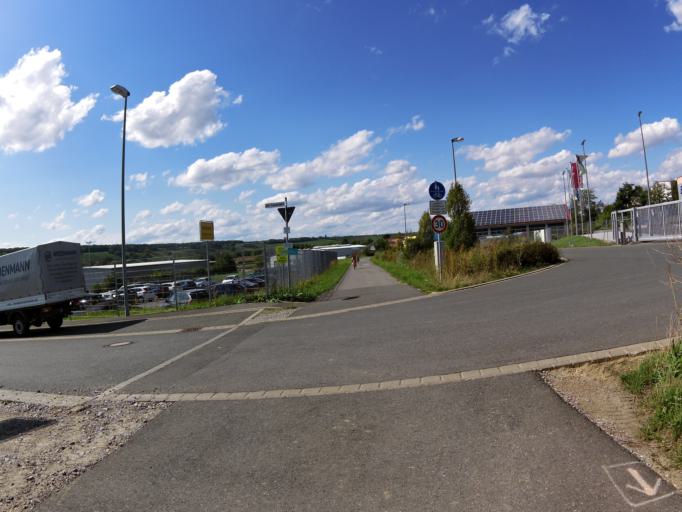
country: DE
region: Bavaria
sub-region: Regierungsbezirk Unterfranken
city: Marktsteft
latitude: 49.6875
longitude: 10.1467
